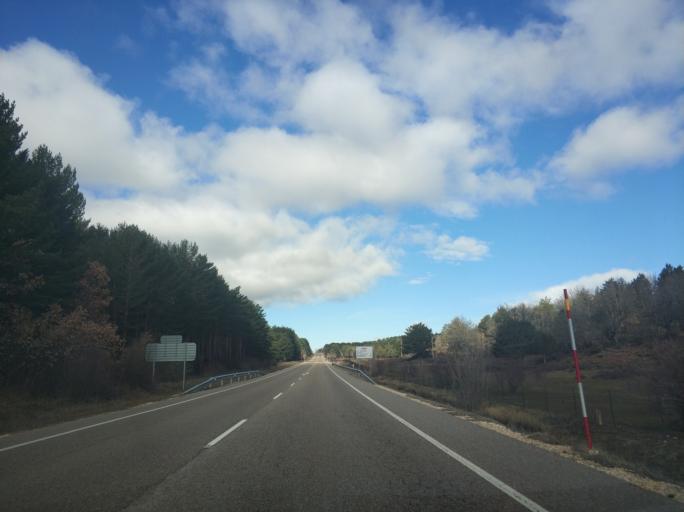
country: ES
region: Castille and Leon
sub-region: Provincia de Burgos
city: Rabanera del Pinar
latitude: 41.8860
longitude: -3.2342
